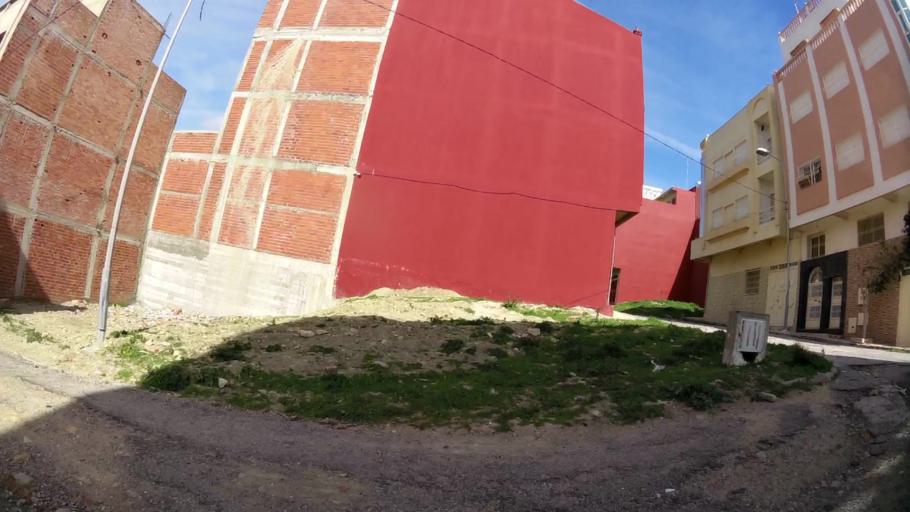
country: MA
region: Tanger-Tetouan
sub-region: Tanger-Assilah
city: Tangier
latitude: 35.7670
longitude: -5.7732
